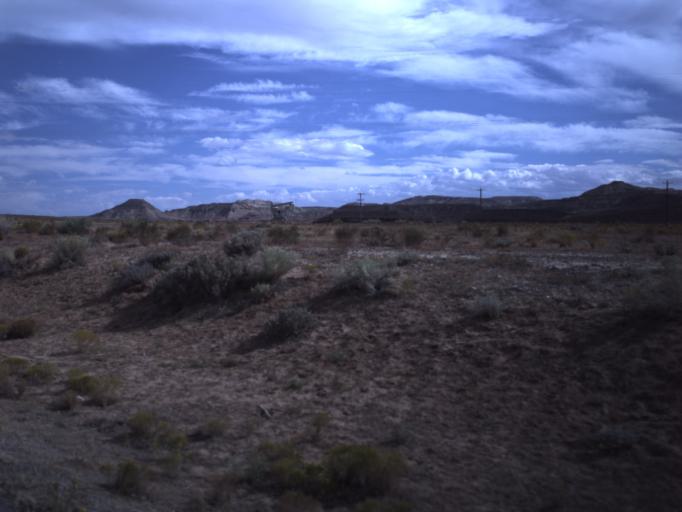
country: US
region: Utah
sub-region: San Juan County
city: Blanding
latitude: 37.2420
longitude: -109.2461
